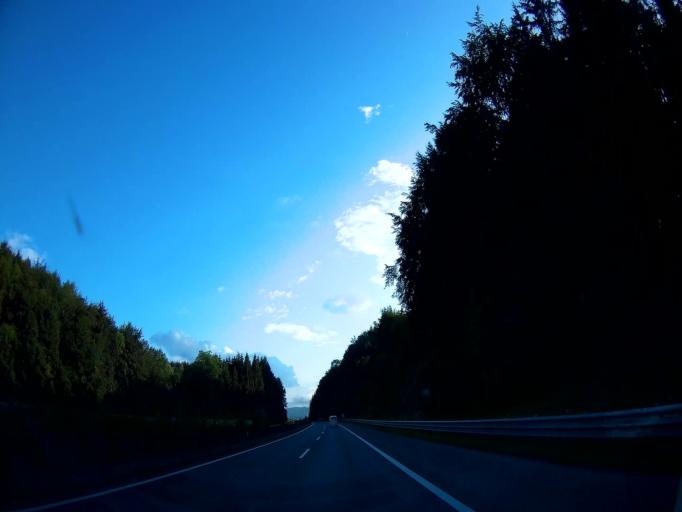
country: AT
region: Upper Austria
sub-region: Politischer Bezirk Vocklabruck
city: Desselbrunn
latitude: 47.9907
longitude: 13.7823
